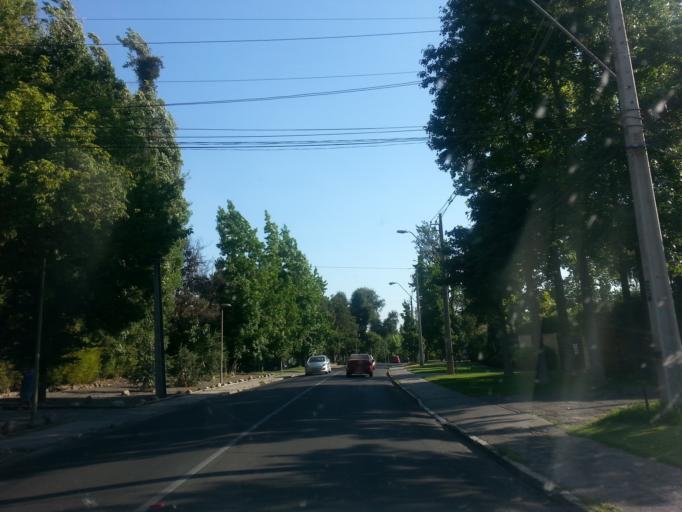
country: CL
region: Santiago Metropolitan
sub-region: Provincia de Santiago
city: Villa Presidente Frei, Nunoa, Santiago, Chile
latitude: -33.3979
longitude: -70.5316
